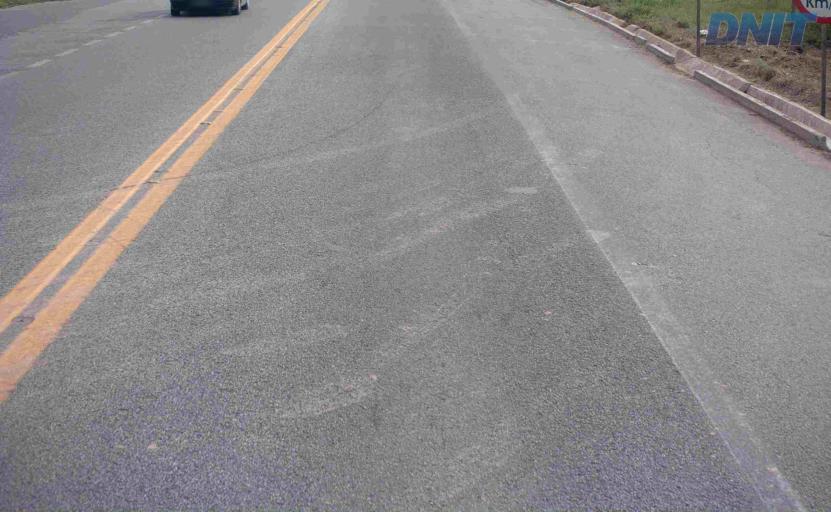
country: BR
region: Minas Gerais
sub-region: Santa Luzia
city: Santa Luzia
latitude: -19.8343
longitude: -43.8509
